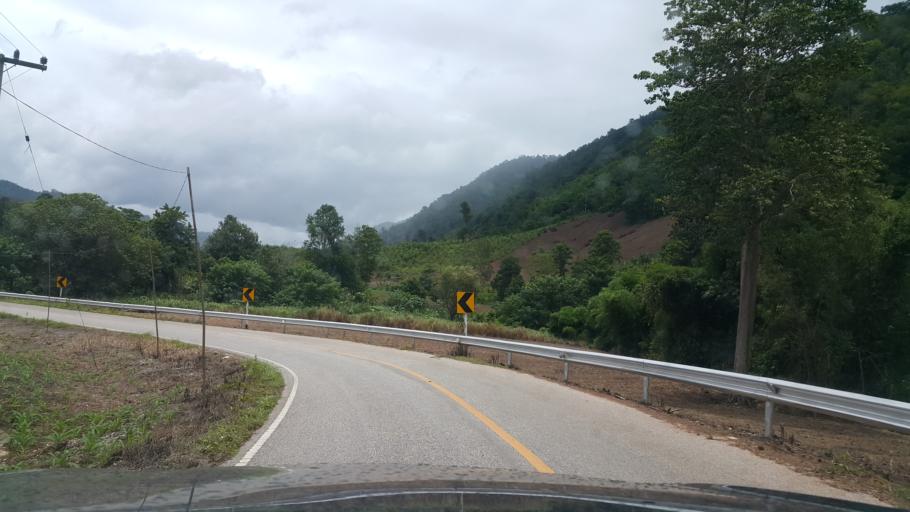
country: TH
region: Loei
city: Na Haeo
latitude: 17.5504
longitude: 100.8426
